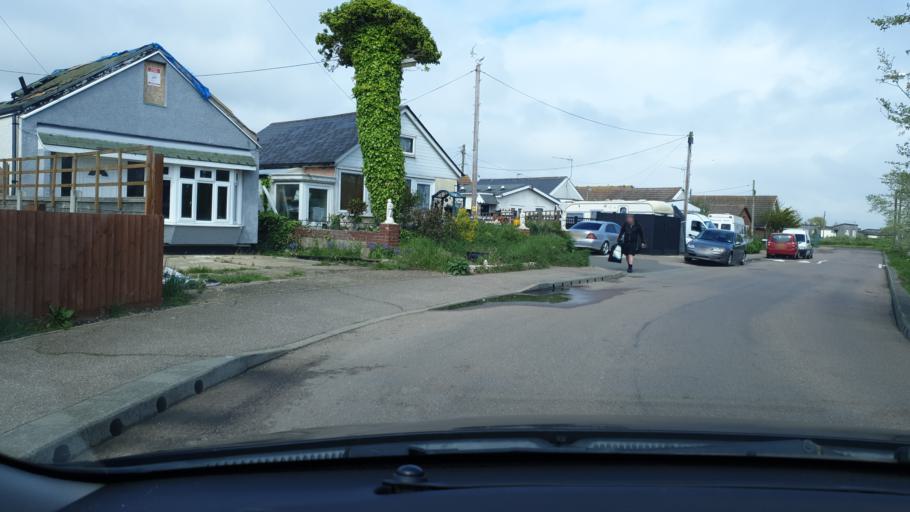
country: GB
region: England
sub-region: Essex
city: Saint Osyth
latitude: 51.7742
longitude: 1.1011
